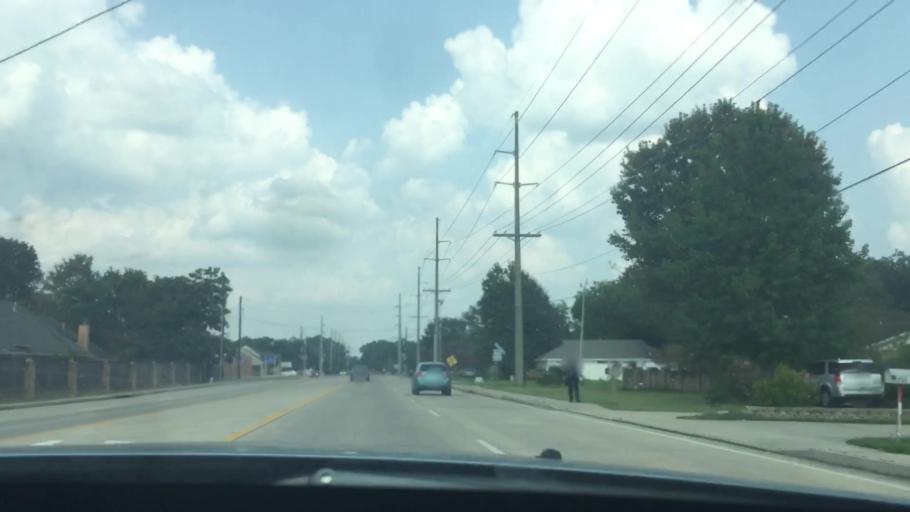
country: US
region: Louisiana
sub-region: East Baton Rouge Parish
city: Westminster
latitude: 30.4393
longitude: -91.0493
